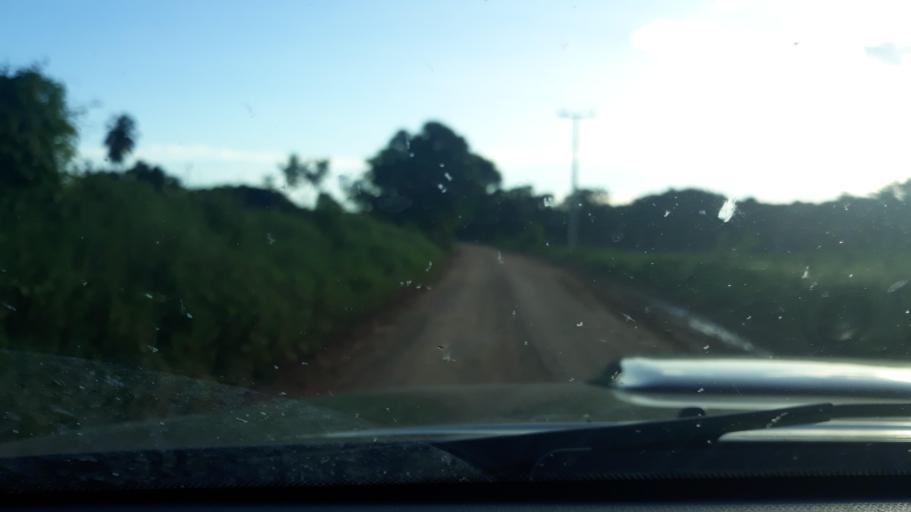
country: BR
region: Bahia
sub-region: Riacho De Santana
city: Riacho de Santana
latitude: -13.8288
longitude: -42.7289
